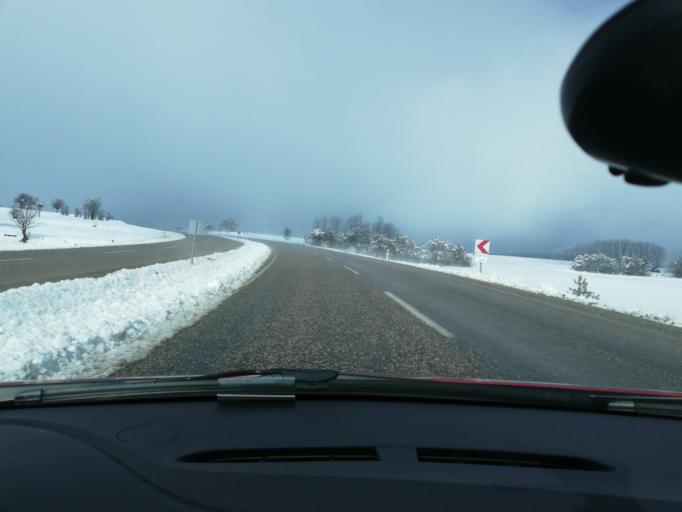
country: TR
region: Kastamonu
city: Ihsangazi
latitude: 41.3070
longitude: 33.5755
